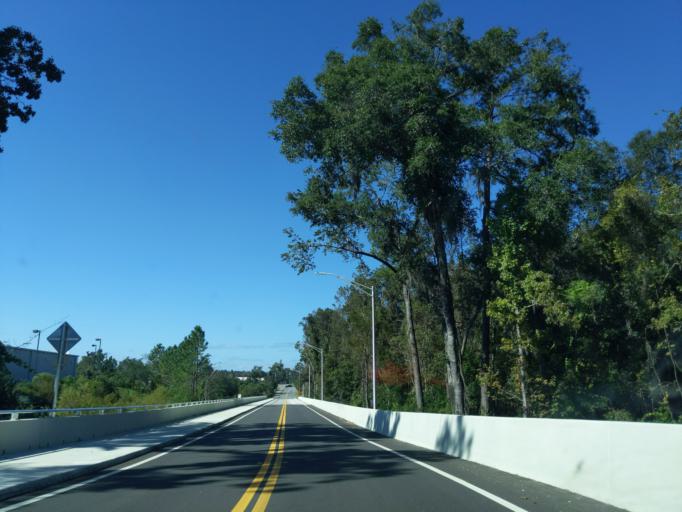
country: US
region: Florida
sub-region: Leon County
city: Tallahassee
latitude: 30.4637
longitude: -84.2234
